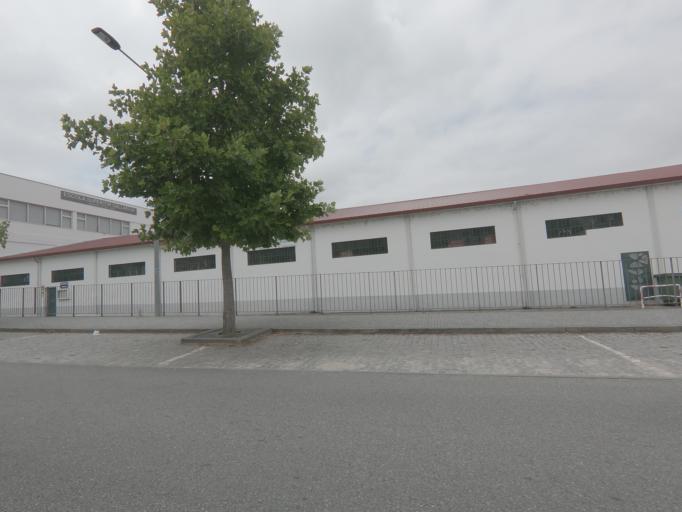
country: PT
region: Viana do Castelo
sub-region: Vila Nova de Cerveira
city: Vila Nova de Cerveira
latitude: 41.9454
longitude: -8.7425
